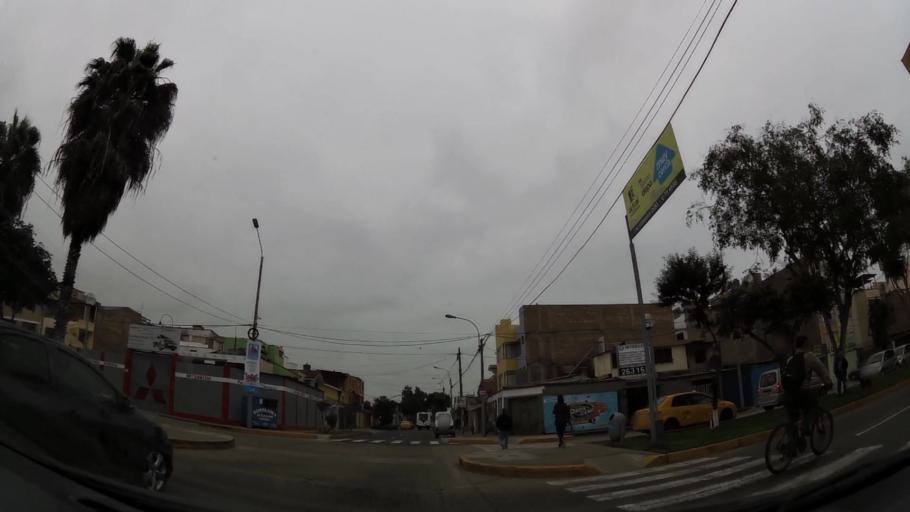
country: PE
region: Lima
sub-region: Lima
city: San Isidro
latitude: -12.0869
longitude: -77.0839
